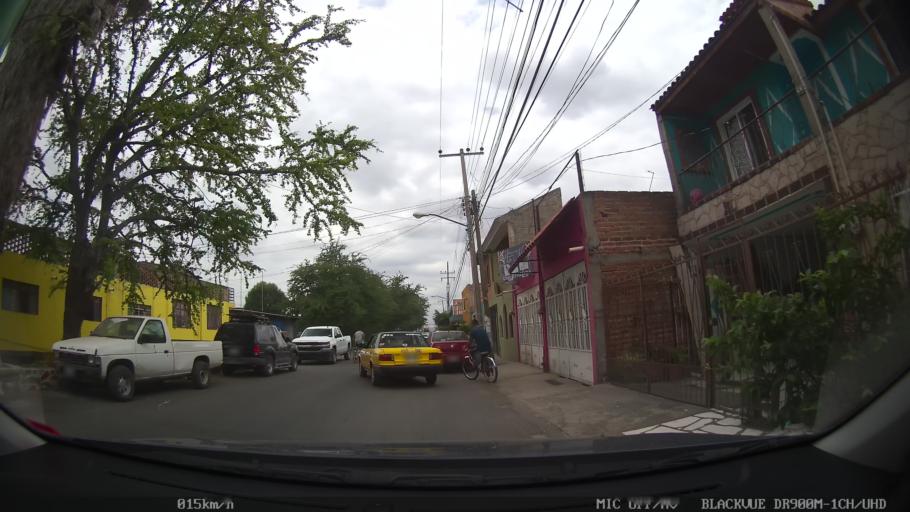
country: MX
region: Jalisco
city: Tonala
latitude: 20.6533
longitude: -103.2556
